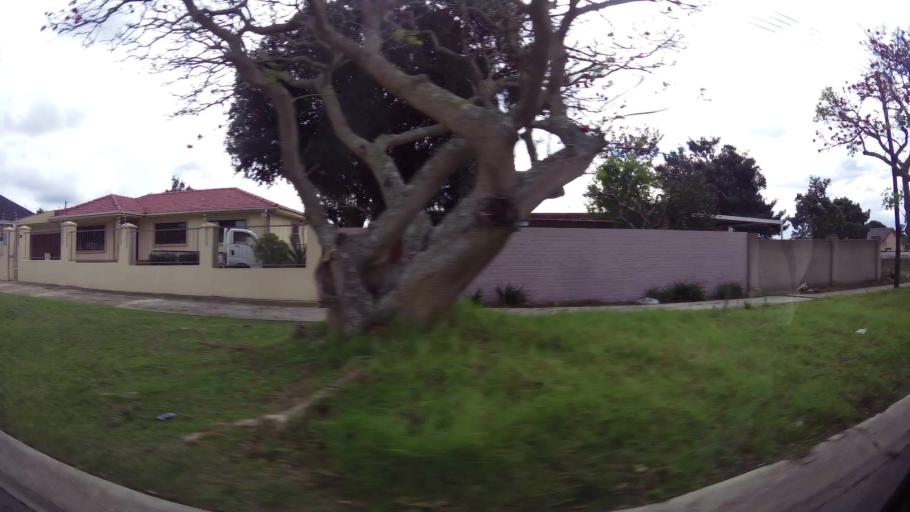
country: ZA
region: Eastern Cape
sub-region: Nelson Mandela Bay Metropolitan Municipality
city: Port Elizabeth
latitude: -33.9420
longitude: 25.5192
